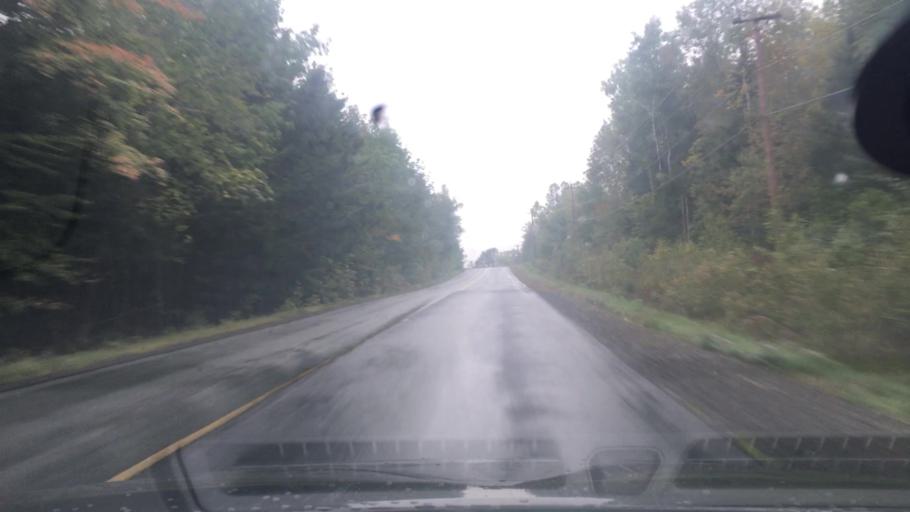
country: CA
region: Nova Scotia
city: Windsor
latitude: 44.8365
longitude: -64.2514
